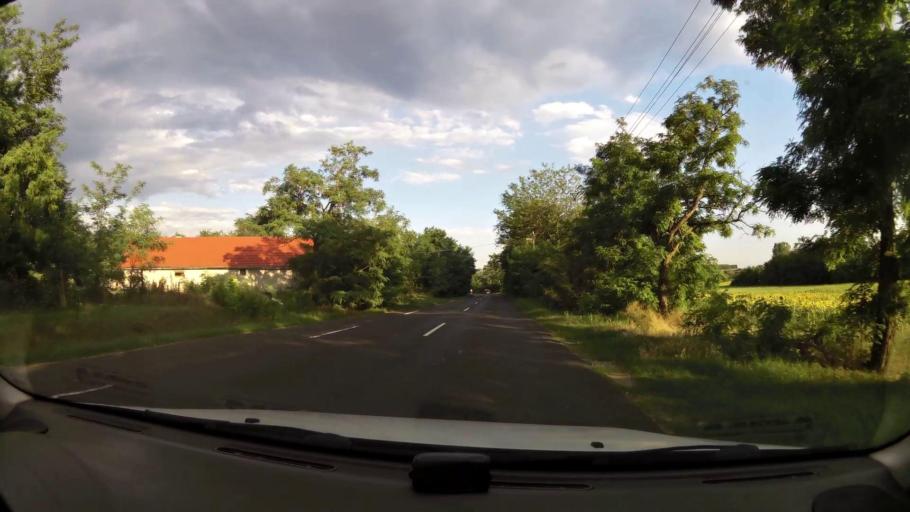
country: HU
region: Pest
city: Tapiosag
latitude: 47.4128
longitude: 19.6107
